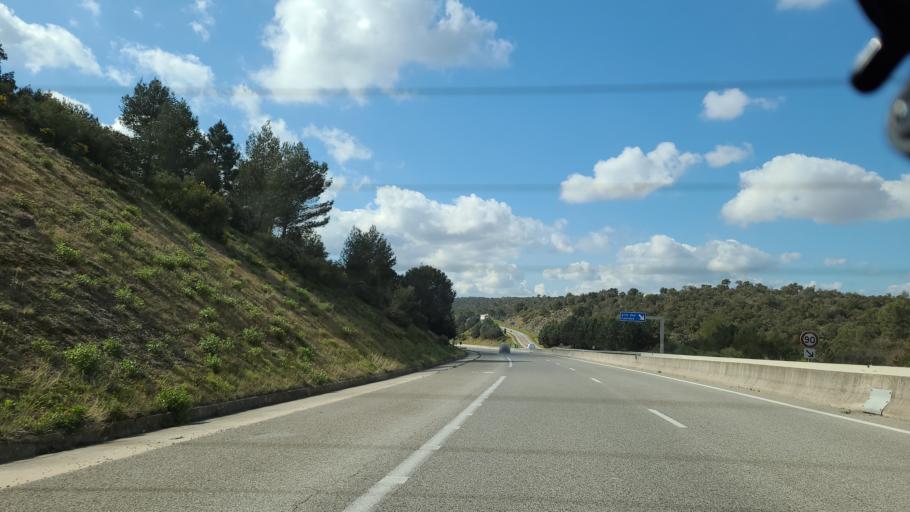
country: FR
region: Provence-Alpes-Cote d'Azur
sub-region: Departement du Var
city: Carnoules
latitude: 43.2872
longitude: 6.1907
